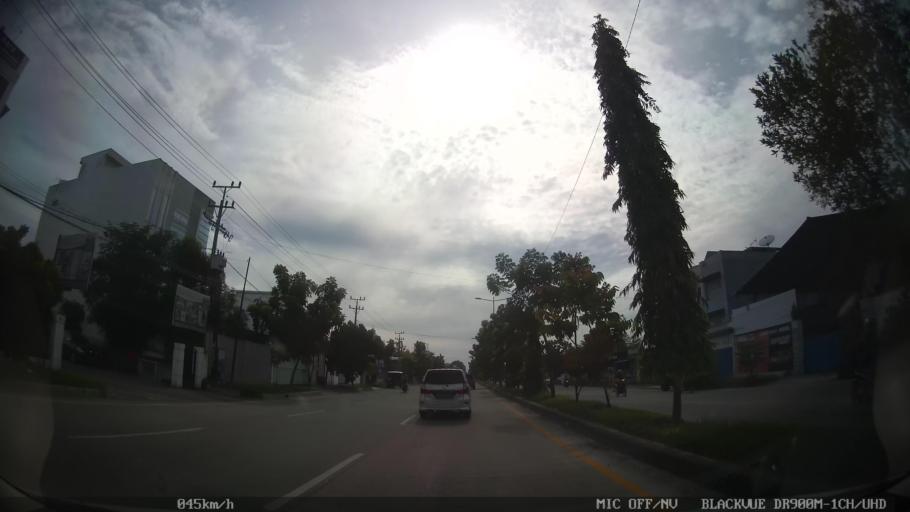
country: ID
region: North Sumatra
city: Medan
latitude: 3.6294
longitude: 98.6875
